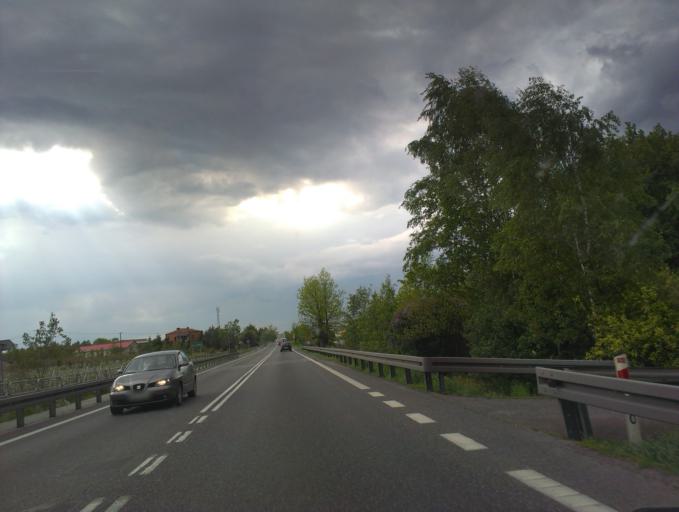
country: PL
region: Masovian Voivodeship
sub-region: Powiat grojecki
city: Pniewy
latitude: 51.9066
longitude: 20.7469
